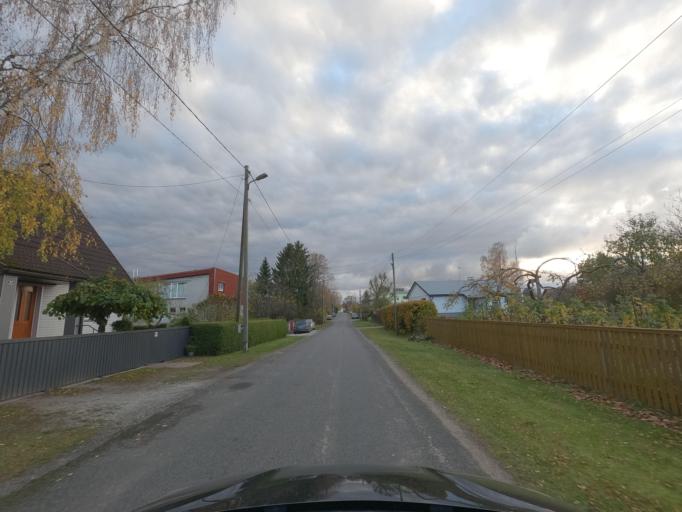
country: EE
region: Harju
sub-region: Saue linn
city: Saue
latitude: 59.3202
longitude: 24.5463
